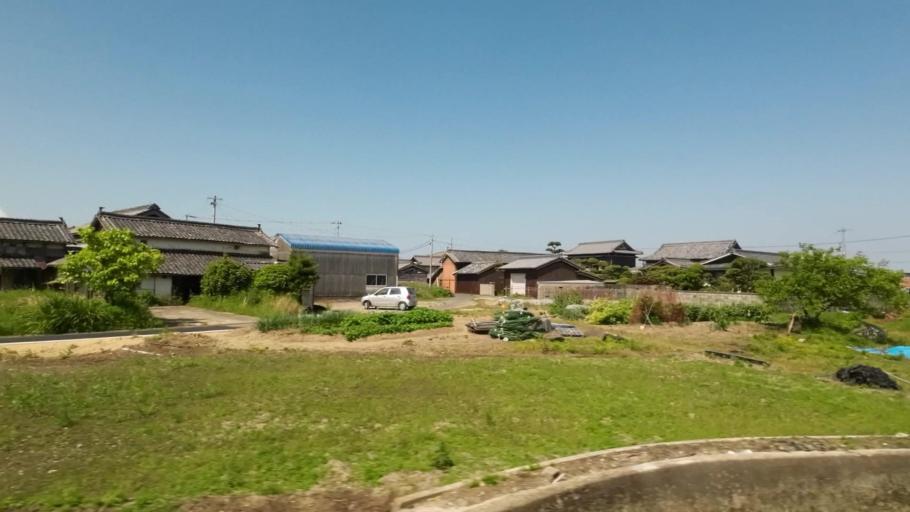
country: JP
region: Kagawa
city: Kan'onjicho
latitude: 34.1100
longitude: 133.6494
